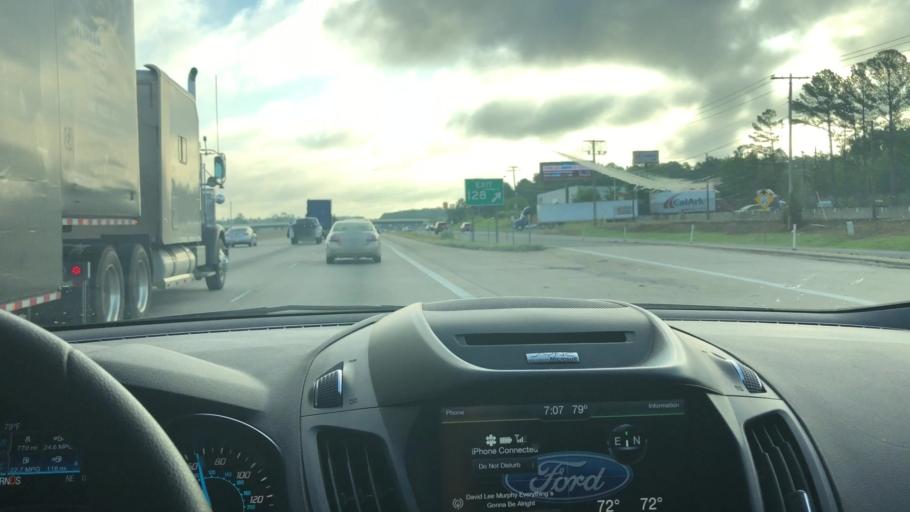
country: US
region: Arkansas
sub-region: Pulaski County
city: Alexander
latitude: 34.6528
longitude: -92.4130
